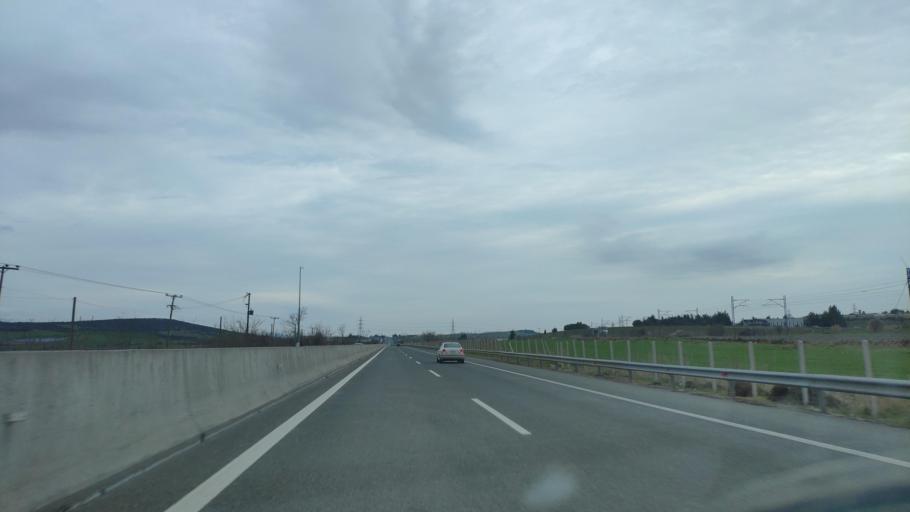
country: GR
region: Central Greece
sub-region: Nomos Voiotias
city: Arma
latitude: 38.3771
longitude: 23.4525
